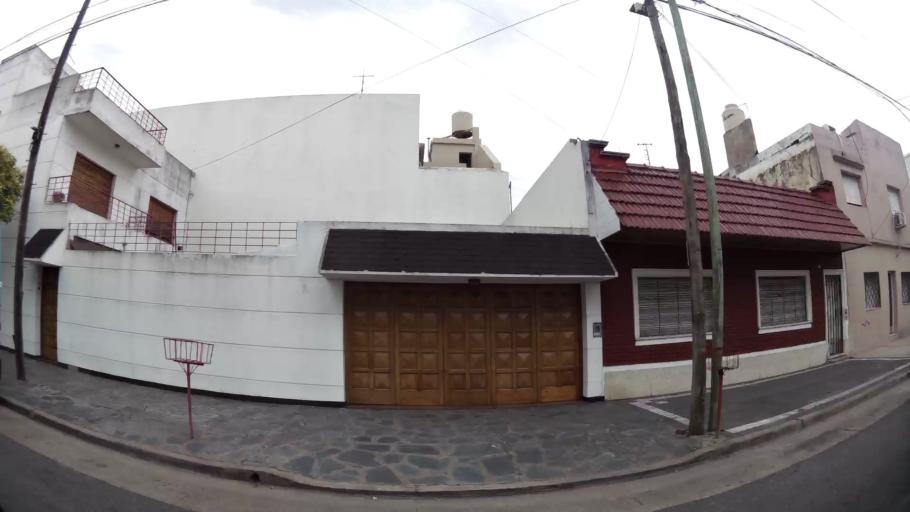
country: AR
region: Buenos Aires
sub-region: Partido de Avellaneda
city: Avellaneda
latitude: -34.6761
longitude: -58.3875
